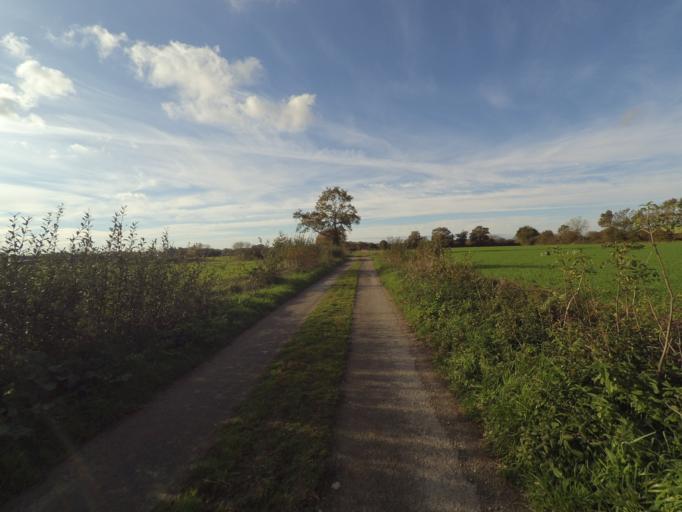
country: FR
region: Pays de la Loire
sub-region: Departement de la Vendee
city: Saint-Hilaire-de-Loulay
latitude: 47.0088
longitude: -1.3511
